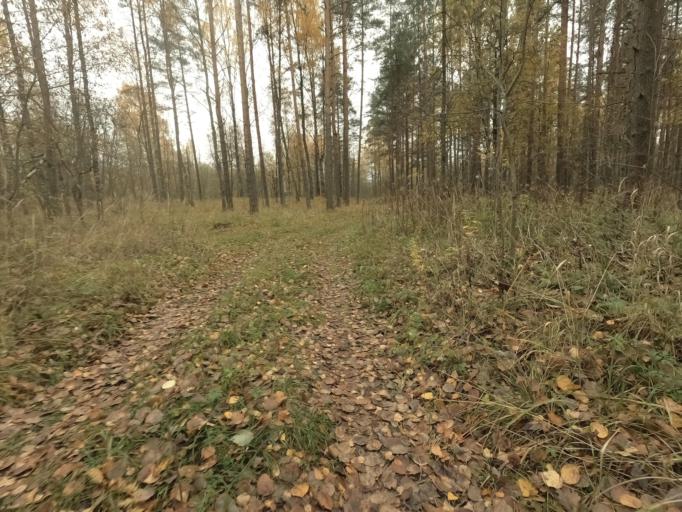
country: RU
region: Leningrad
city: Kirovsk
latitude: 59.8590
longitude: 30.9998
